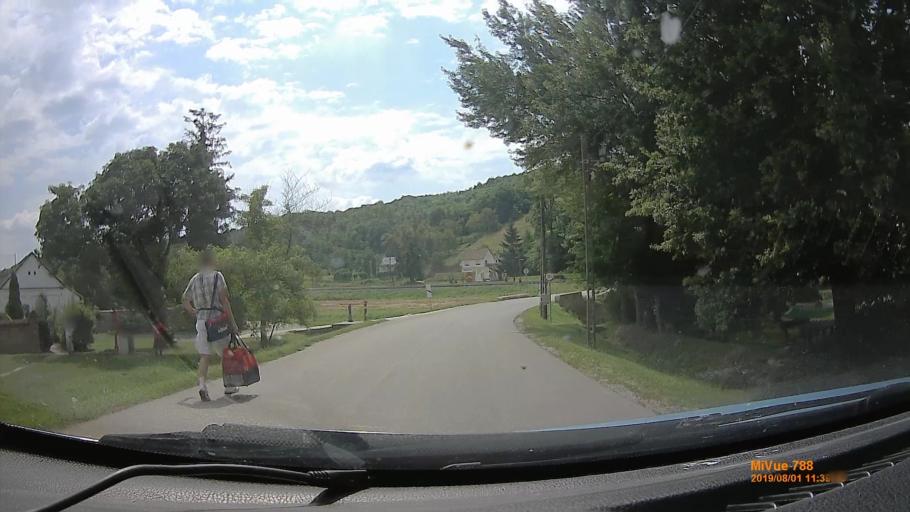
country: HU
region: Baranya
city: Villany
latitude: 45.8924
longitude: 18.3935
